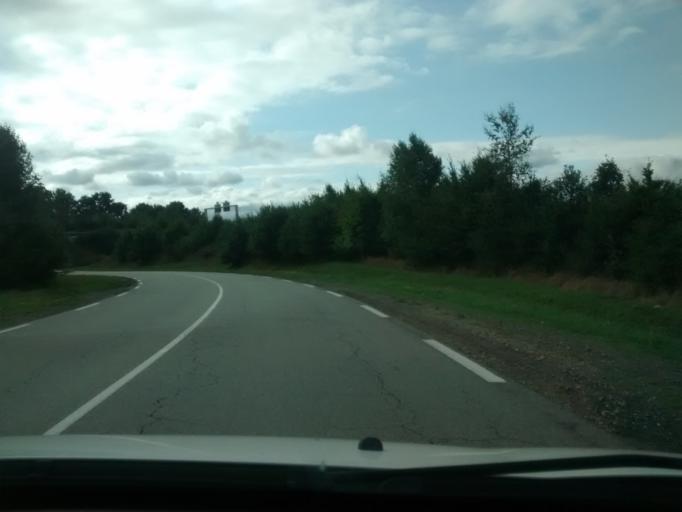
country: FR
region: Brittany
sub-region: Departement d'Ille-et-Vilaine
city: Cesson-Sevigne
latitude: 48.1194
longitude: -1.5698
